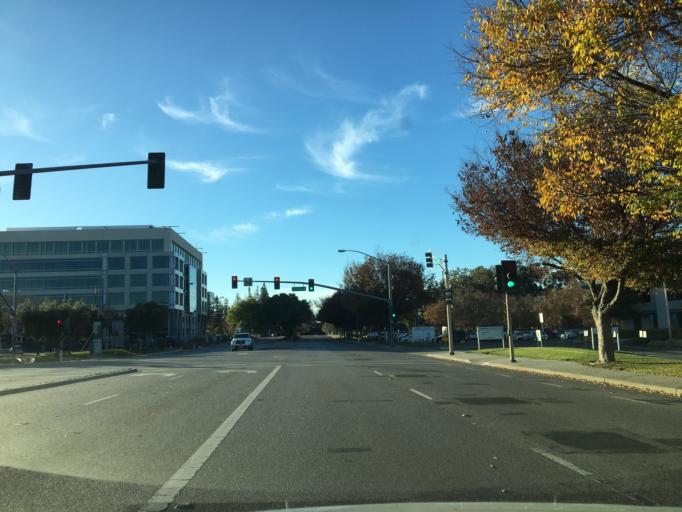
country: US
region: California
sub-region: Santa Clara County
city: Santa Clara
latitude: 37.3889
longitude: -121.9660
